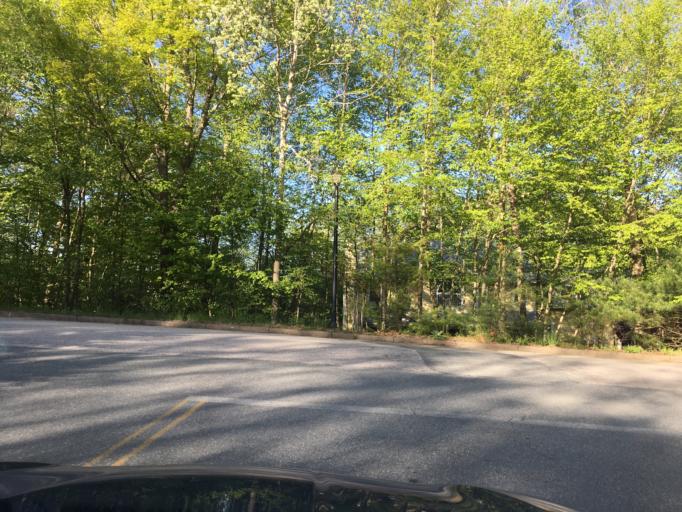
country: US
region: Rhode Island
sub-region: Washington County
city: Exeter
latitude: 41.6104
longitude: -71.5206
